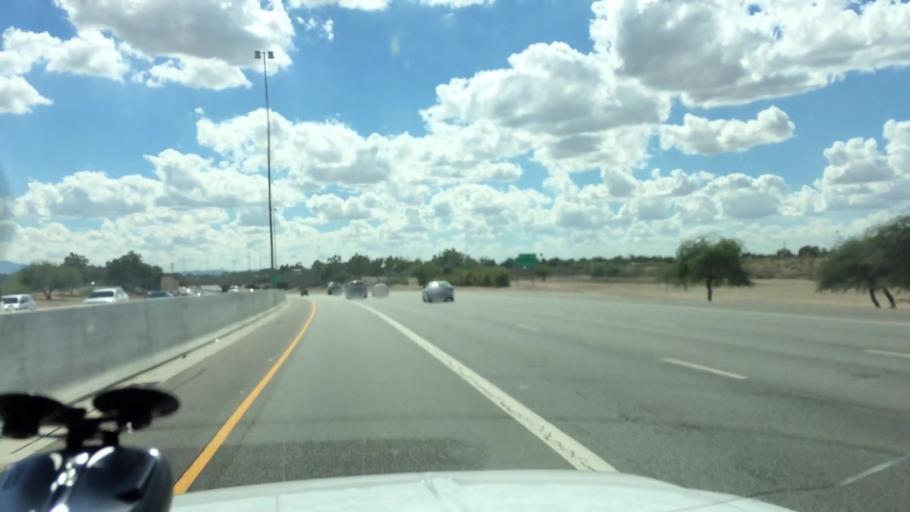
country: US
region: Arizona
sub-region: Maricopa County
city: Sun City
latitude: 33.5978
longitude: -112.2588
